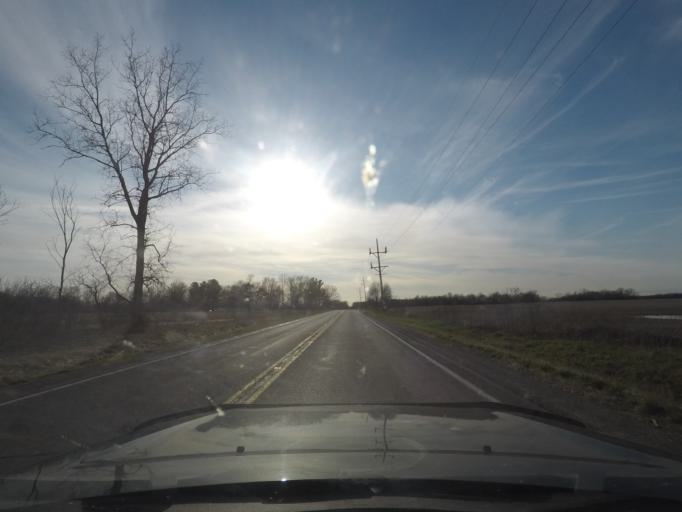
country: US
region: Indiana
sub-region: Saint Joseph County
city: Walkerton
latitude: 41.4481
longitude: -86.4064
